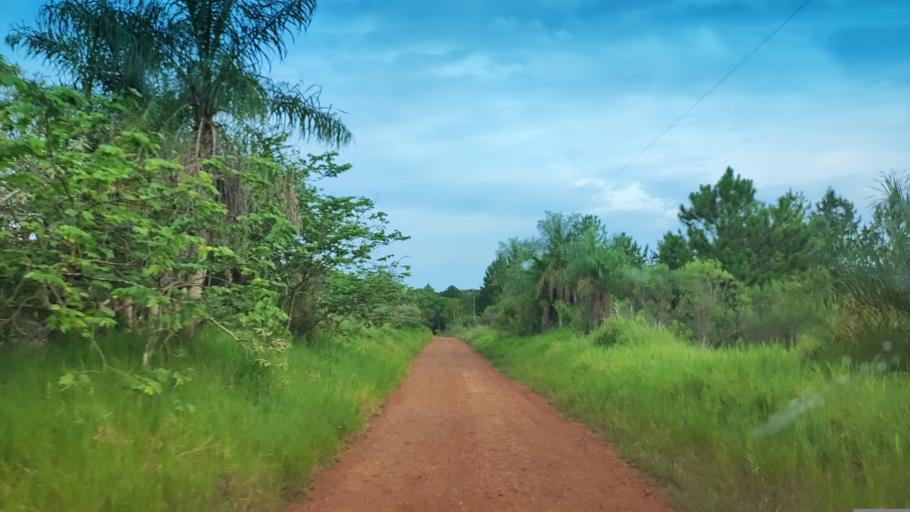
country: AR
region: Misiones
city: Gobernador Roca
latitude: -27.1704
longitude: -55.4506
